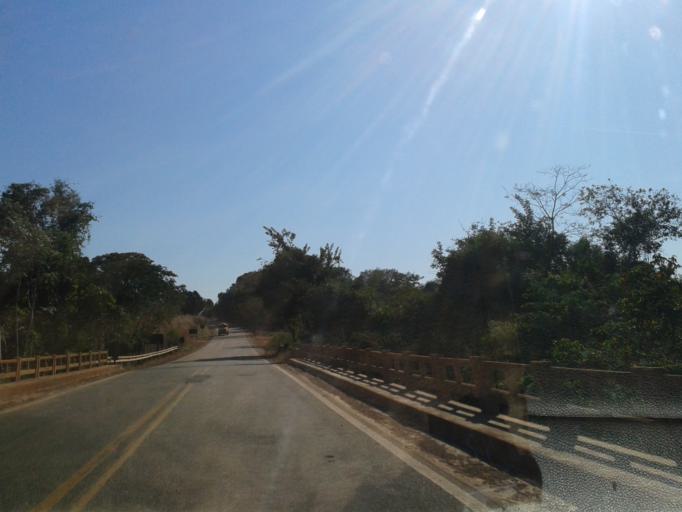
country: BR
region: Goias
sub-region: Mozarlandia
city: Mozarlandia
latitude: -14.6488
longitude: -50.5207
